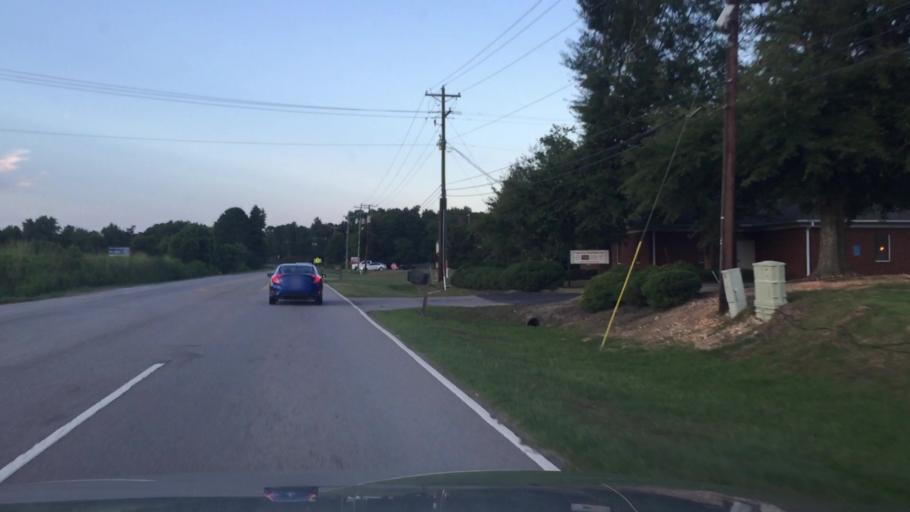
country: US
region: South Carolina
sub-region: Richland County
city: Hopkins
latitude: 33.9505
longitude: -80.9299
